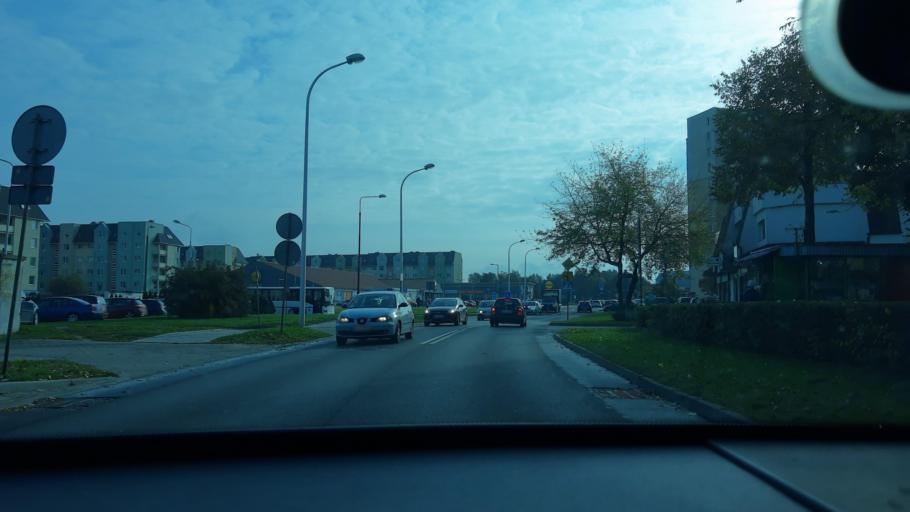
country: PL
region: Lodz Voivodeship
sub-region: Powiat sieradzki
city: Sieradz
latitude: 51.5937
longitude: 18.7240
